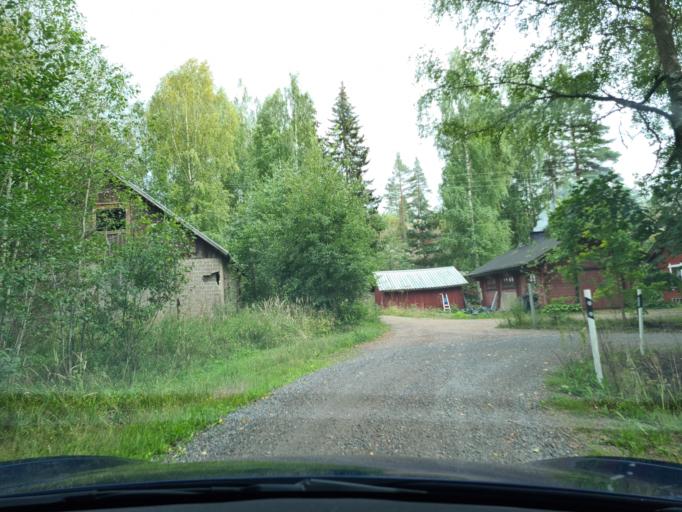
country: FI
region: Uusimaa
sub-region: Helsinki
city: Vihti
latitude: 60.4171
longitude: 24.4977
